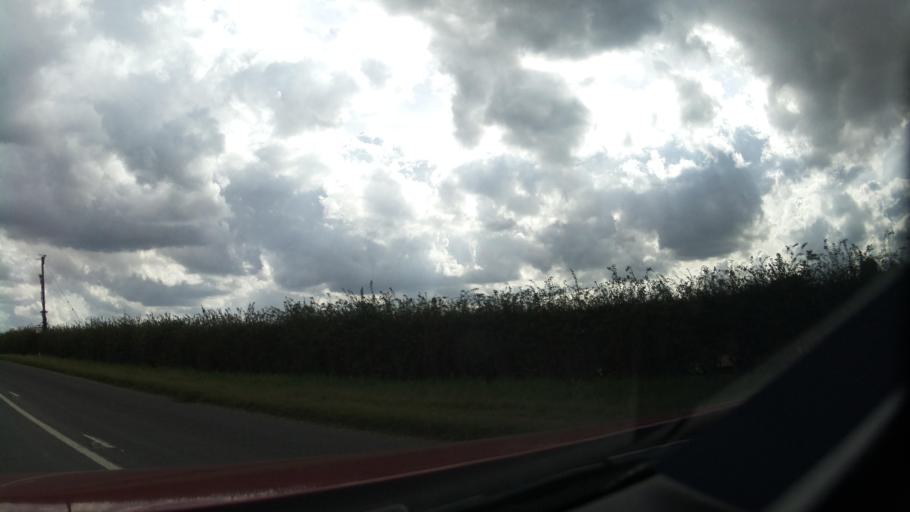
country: GB
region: England
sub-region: North Yorkshire
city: Ripon
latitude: 54.1725
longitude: -1.5527
